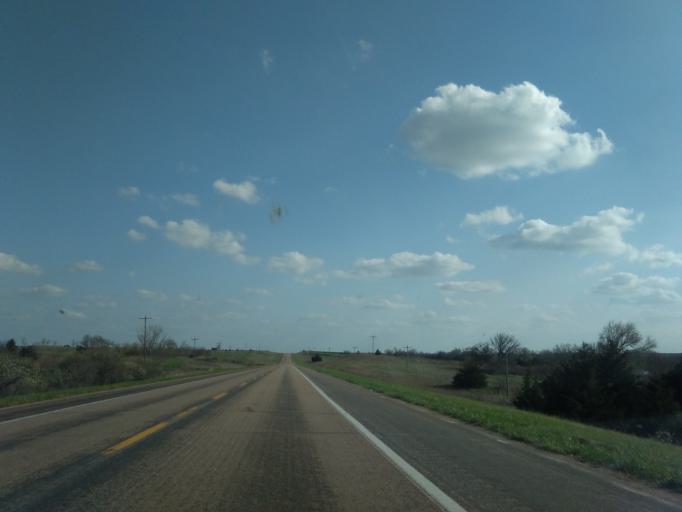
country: US
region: Nebraska
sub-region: Webster County
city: Red Cloud
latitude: 40.1364
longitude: -98.5190
